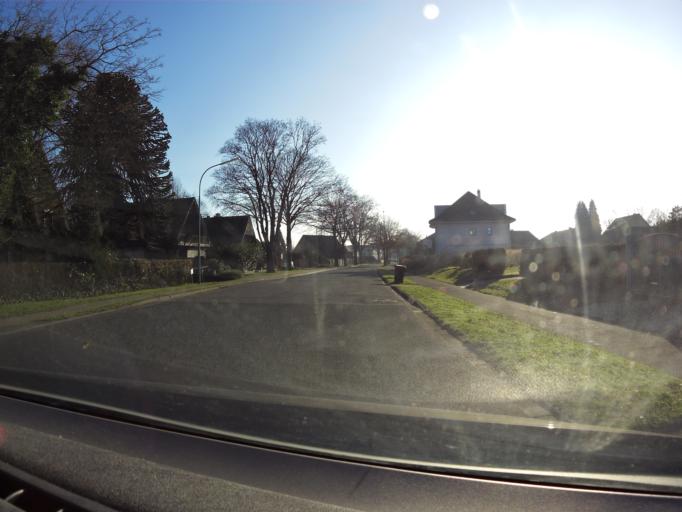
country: DE
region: North Rhine-Westphalia
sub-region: Regierungsbezirk Dusseldorf
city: Bruggen
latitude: 51.2497
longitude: 6.1841
